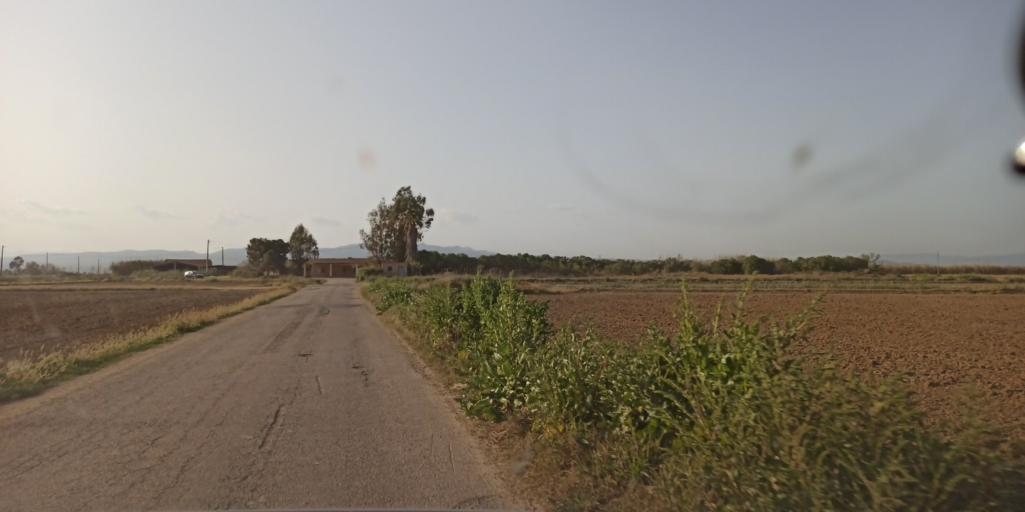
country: ES
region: Catalonia
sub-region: Provincia de Tarragona
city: Deltebre
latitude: 40.7507
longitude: 0.7622
